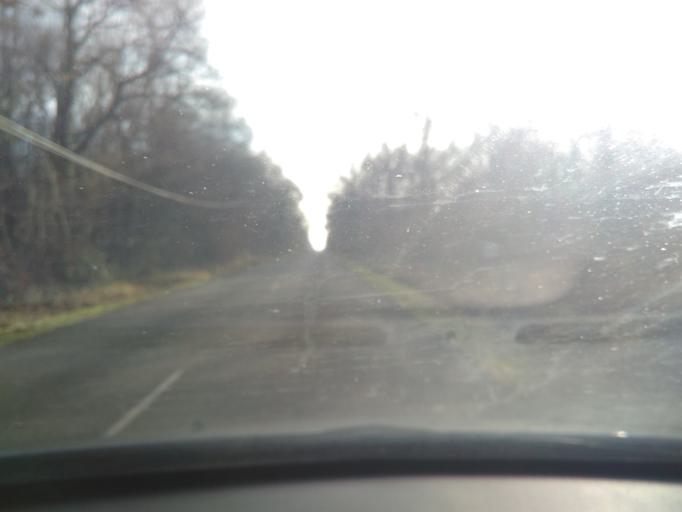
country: FR
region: Bourgogne
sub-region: Departement de la Nievre
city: Chantenay-Saint-Imbert
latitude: 46.7919
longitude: 3.2729
